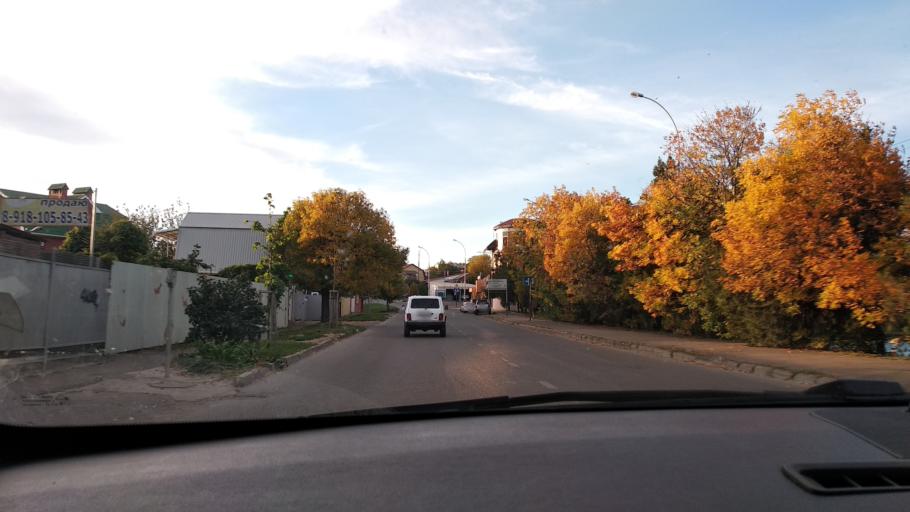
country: RU
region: Krasnodarskiy
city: Krasnodar
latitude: 45.0250
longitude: 38.9879
